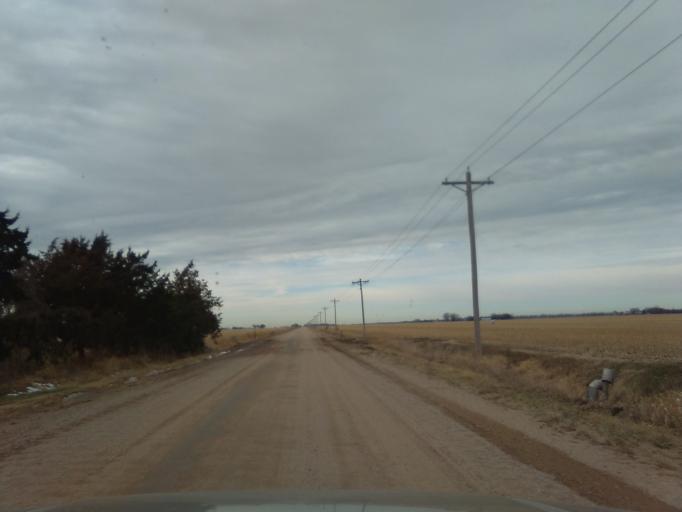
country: US
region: Nebraska
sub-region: Buffalo County
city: Gibbon
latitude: 40.6408
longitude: -98.8977
